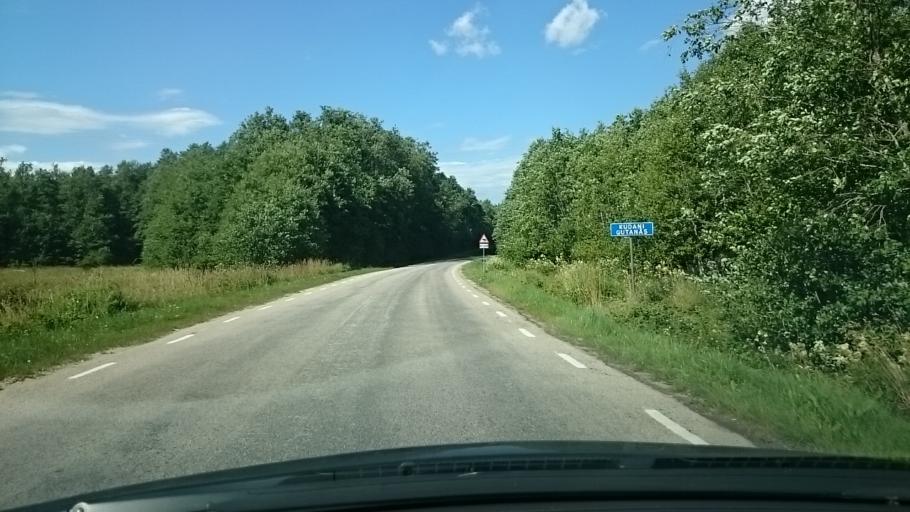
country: EE
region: Laeaene
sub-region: Haapsalu linn
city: Haapsalu
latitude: 59.0431
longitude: 23.5081
